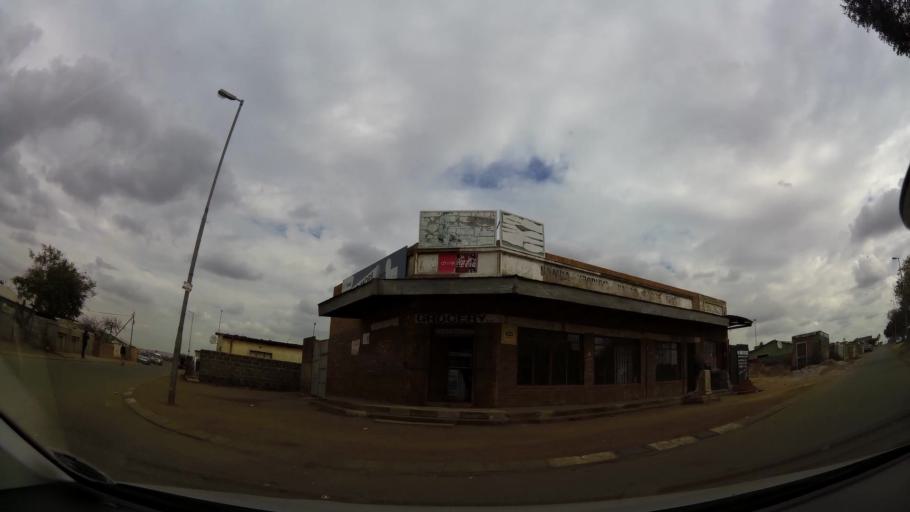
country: ZA
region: Gauteng
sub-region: City of Johannesburg Metropolitan Municipality
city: Soweto
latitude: -26.2760
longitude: 27.8579
